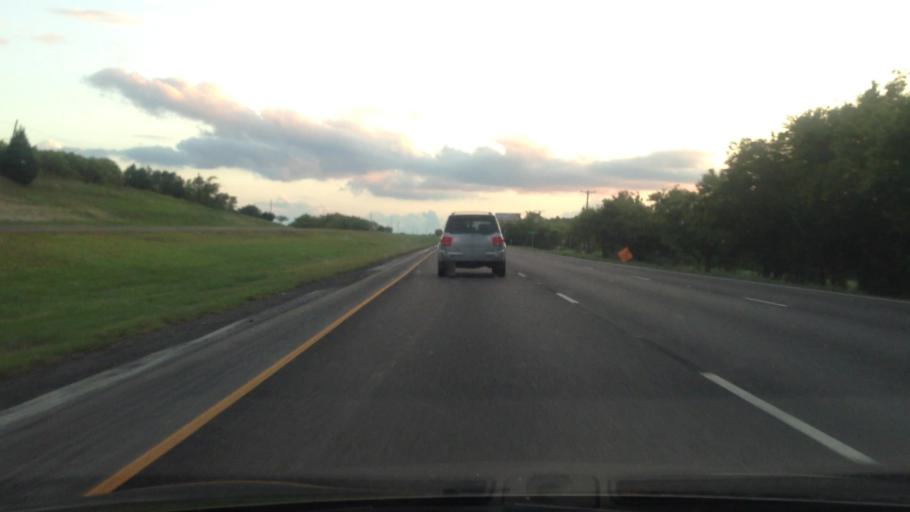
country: US
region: Texas
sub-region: Parker County
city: Aledo
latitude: 32.6094
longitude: -97.5530
